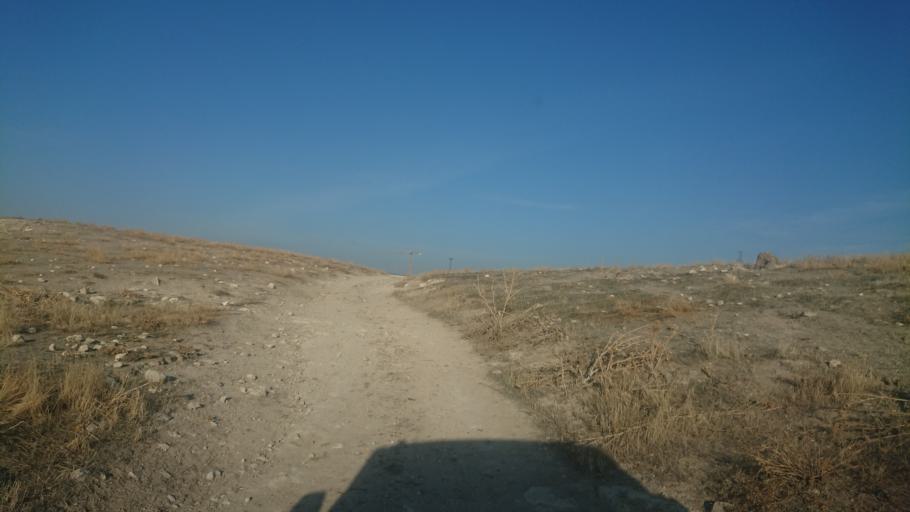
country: TR
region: Aksaray
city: Sultanhani
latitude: 38.1450
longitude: 33.5851
